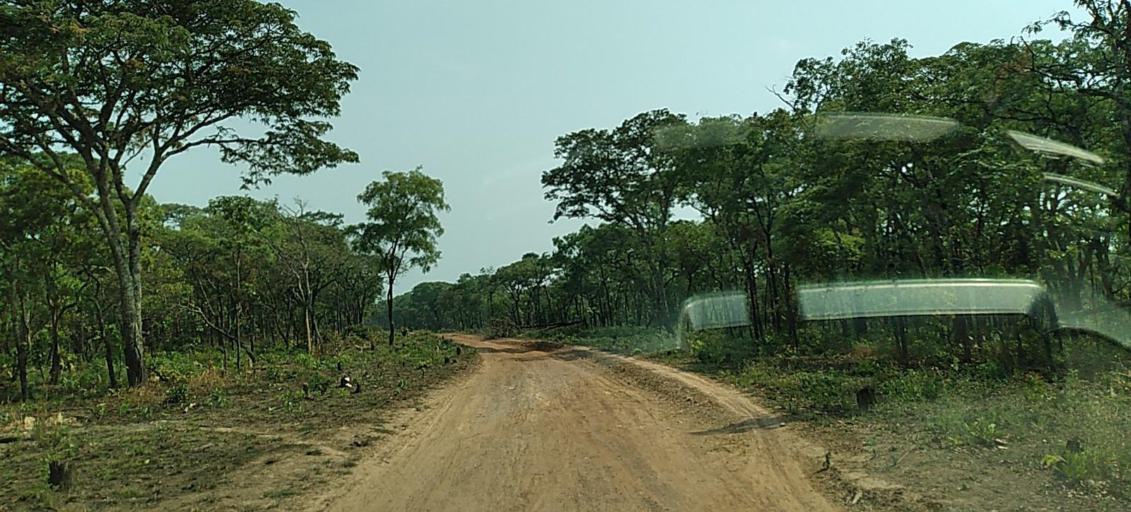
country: ZM
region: North-Western
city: Kansanshi
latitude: -12.0849
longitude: 26.8885
